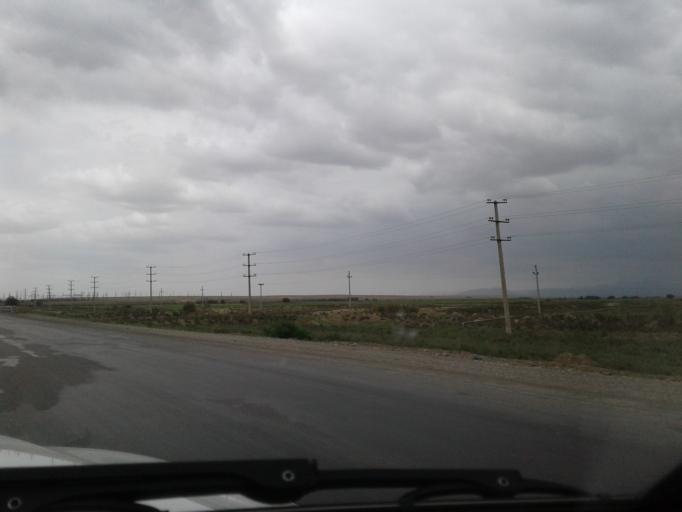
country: TM
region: Ahal
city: Kaka
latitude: 37.3554
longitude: 59.6454
